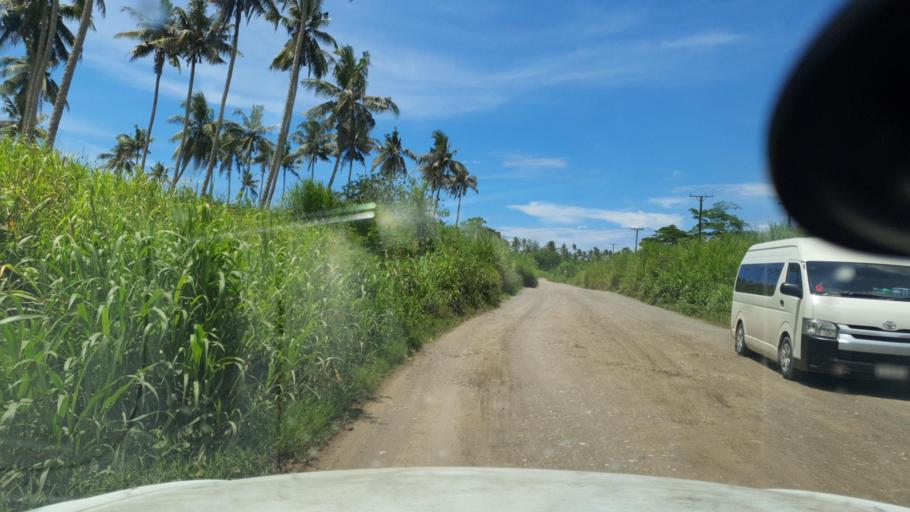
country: SB
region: Guadalcanal
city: Honiara
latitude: -9.4536
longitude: 160.1005
